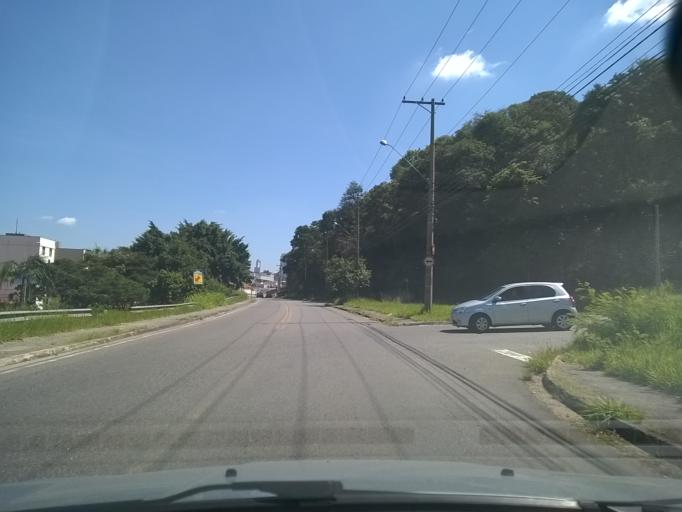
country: BR
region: Sao Paulo
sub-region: Jundiai
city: Jundiai
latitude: -23.2084
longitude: -46.8756
